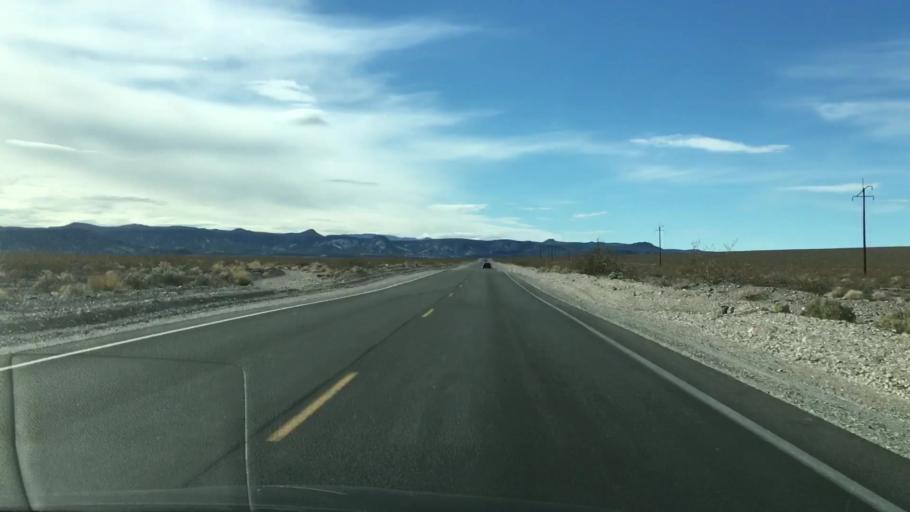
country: US
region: Nevada
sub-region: Nye County
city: Pahrump
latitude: 36.3033
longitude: -116.4836
